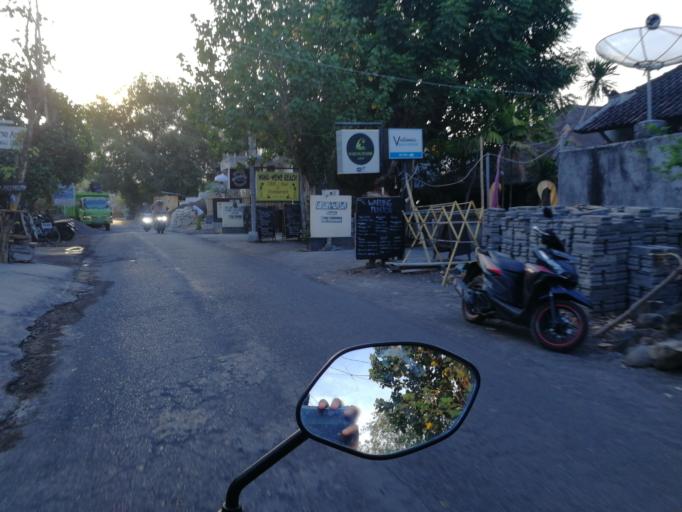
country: ID
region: Bali
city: Biaslantang Kaler
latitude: -8.3355
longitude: 115.6522
